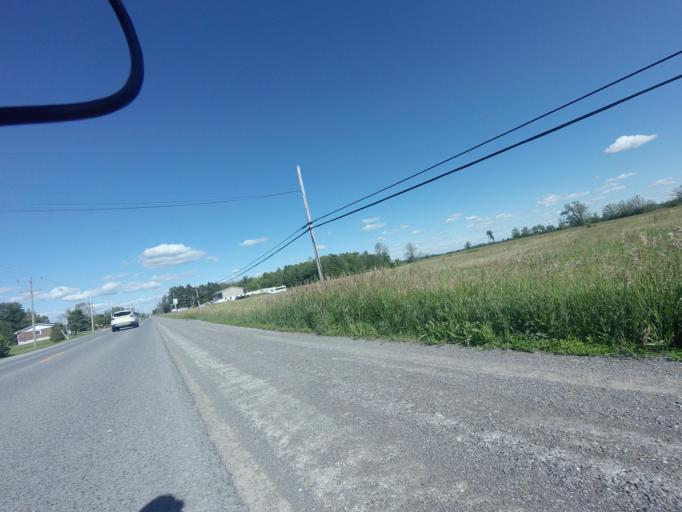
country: CA
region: Ontario
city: Arnprior
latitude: 45.4194
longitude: -76.3954
